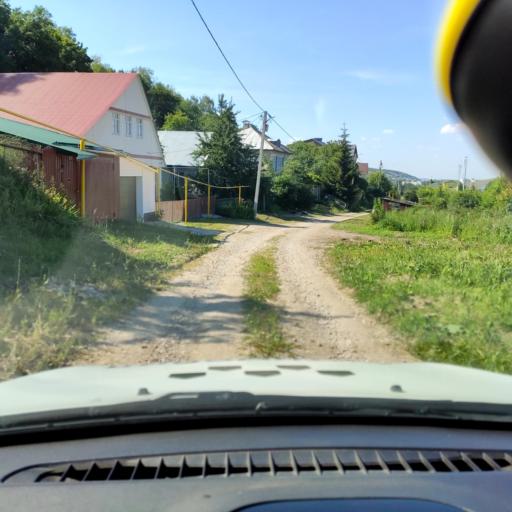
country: RU
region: Samara
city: Zhigulevsk
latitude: 53.3930
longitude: 49.5299
